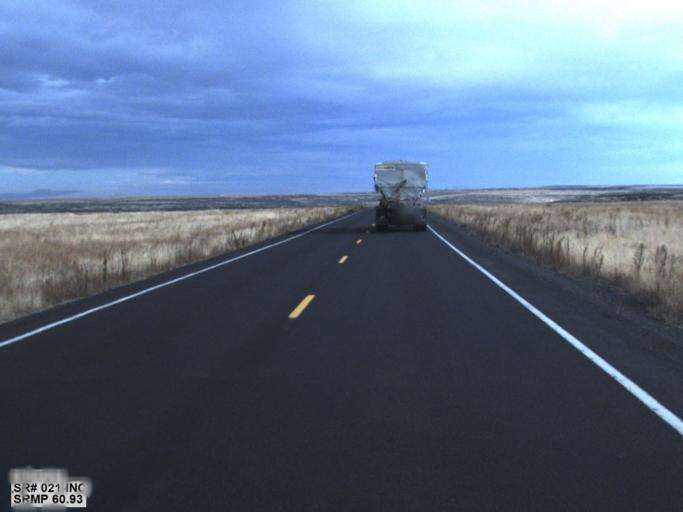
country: US
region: Washington
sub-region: Adams County
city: Ritzville
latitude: 47.3998
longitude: -118.6859
